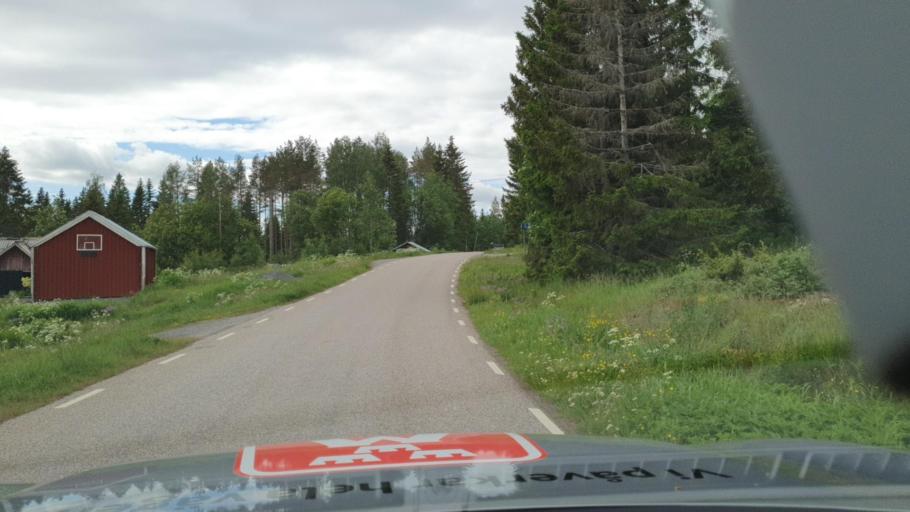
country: SE
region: Vaesternorrland
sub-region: Kramfors Kommun
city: Nordingra
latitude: 62.8622
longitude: 18.3330
